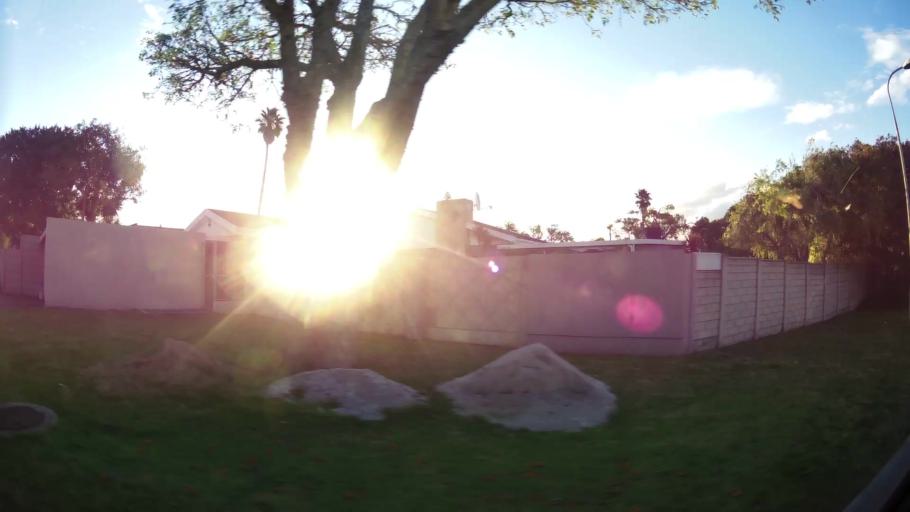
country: ZA
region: Eastern Cape
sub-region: Nelson Mandela Bay Metropolitan Municipality
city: Port Elizabeth
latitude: -33.9740
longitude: 25.5001
